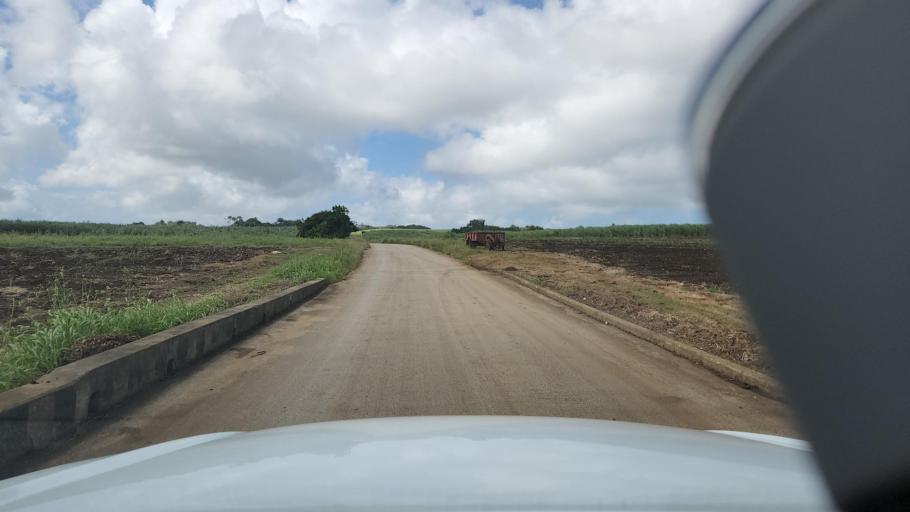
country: BB
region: Saint Joseph
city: Bathsheba
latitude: 13.1950
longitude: -59.5172
